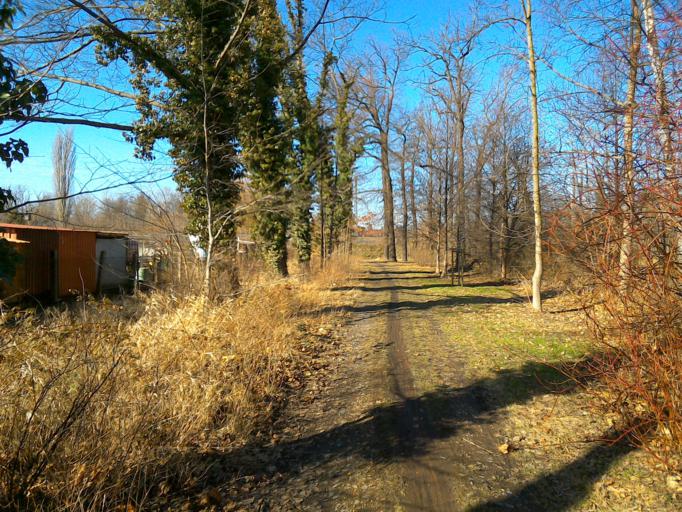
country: DE
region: Saxony
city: Grossenhain
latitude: 51.2930
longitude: 13.5215
